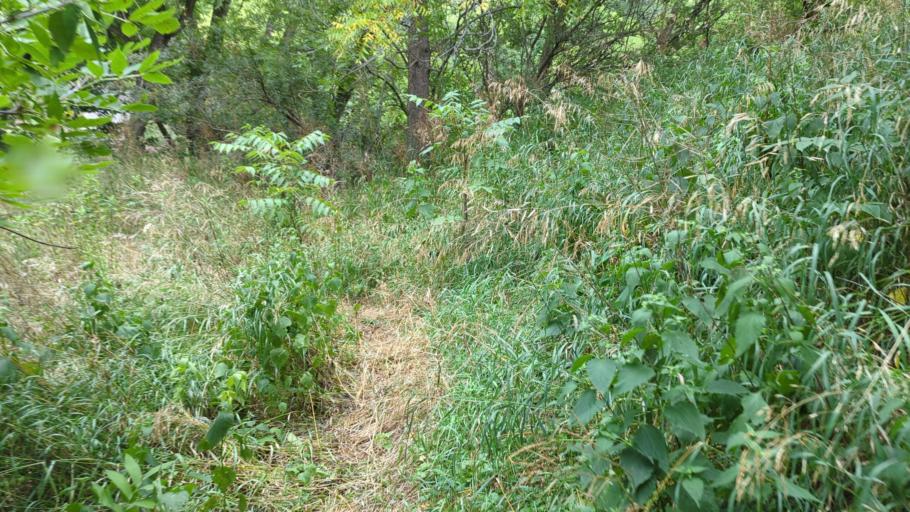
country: US
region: South Dakota
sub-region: Union County
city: Beresford
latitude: 42.9245
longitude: -96.7784
